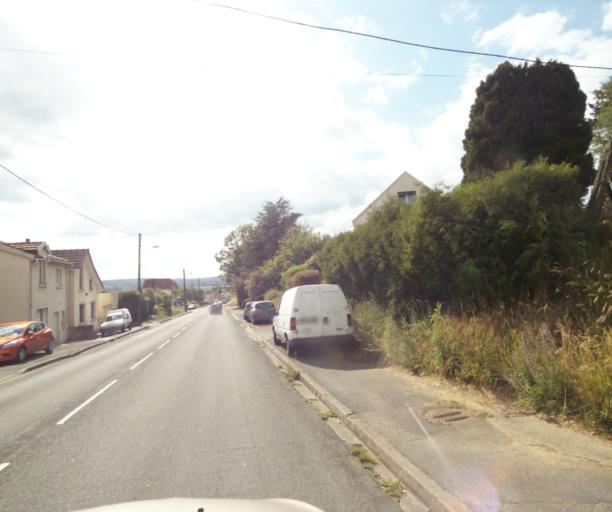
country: FR
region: Champagne-Ardenne
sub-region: Departement des Ardennes
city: Montcy-Notre-Dame
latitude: 49.7602
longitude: 4.7387
